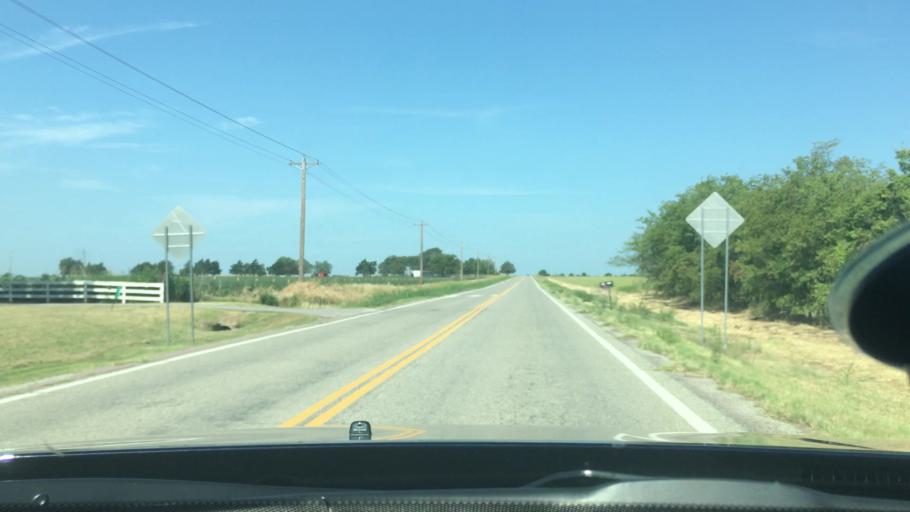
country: US
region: Oklahoma
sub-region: Marshall County
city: Kingston
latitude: 33.9984
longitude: -96.7993
